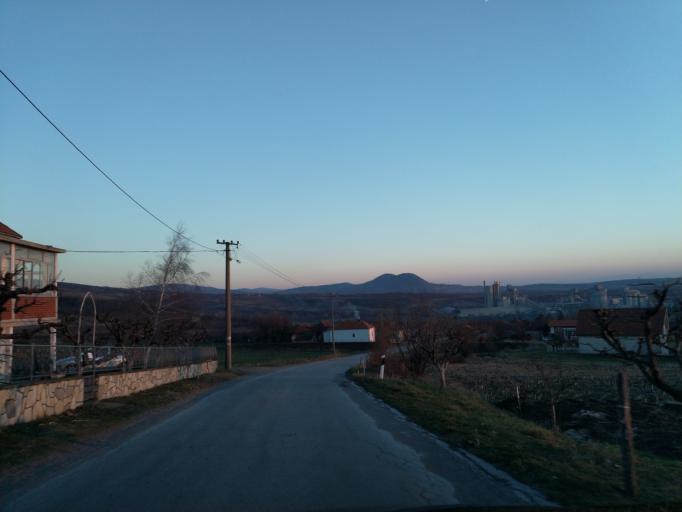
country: RS
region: Central Serbia
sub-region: Pomoravski Okrug
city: Paracin
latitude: 43.9230
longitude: 21.5100
